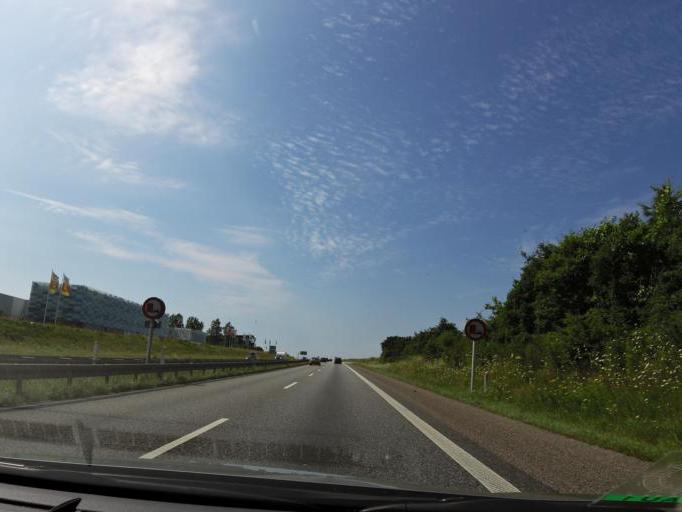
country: DK
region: South Denmark
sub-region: Vejle Kommune
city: Vejle
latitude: 55.7487
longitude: 9.5867
